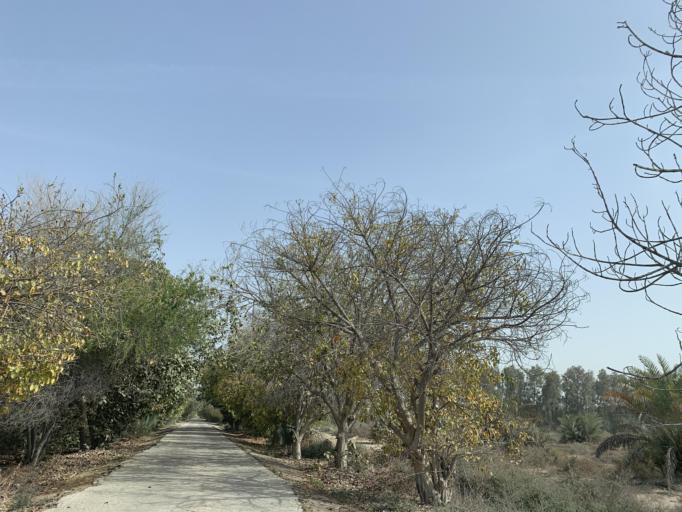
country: BH
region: Northern
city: Madinat `Isa
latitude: 26.1639
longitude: 50.5307
